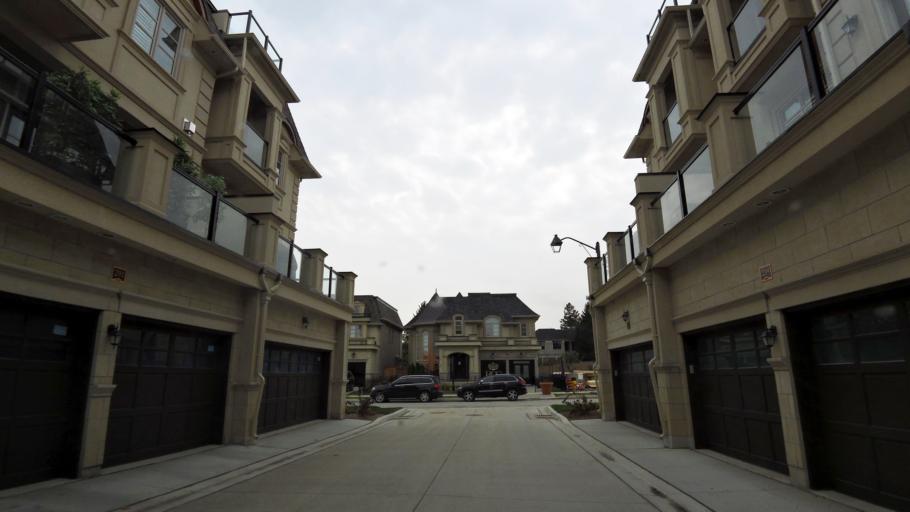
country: CA
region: Ontario
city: Oakville
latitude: 43.4363
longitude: -79.6828
